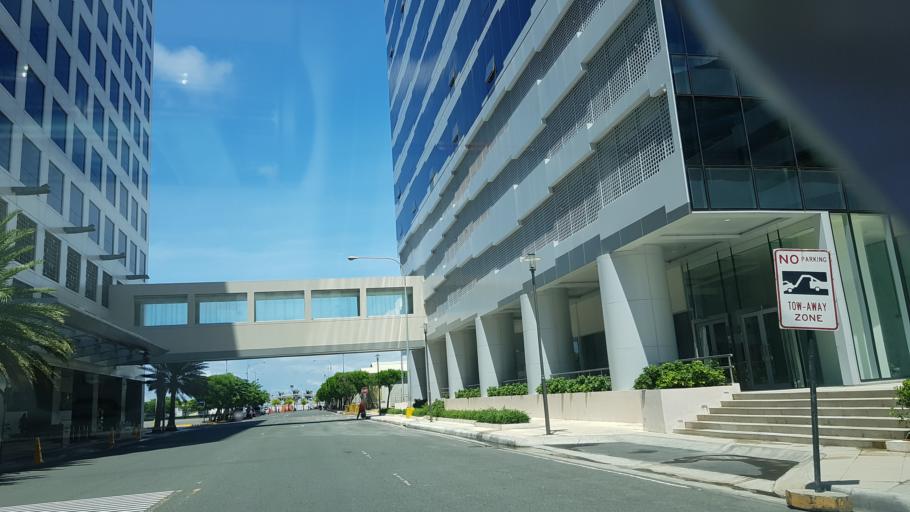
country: PH
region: Metro Manila
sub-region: City of Manila
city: Port Area
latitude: 14.5400
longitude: 120.9816
